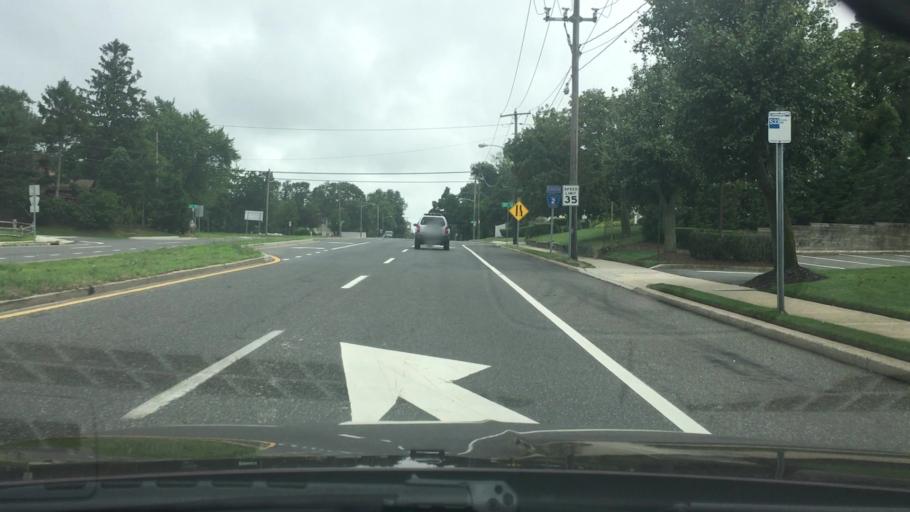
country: US
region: New York
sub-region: Suffolk County
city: North Lindenhurst
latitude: 40.7042
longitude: -73.3872
